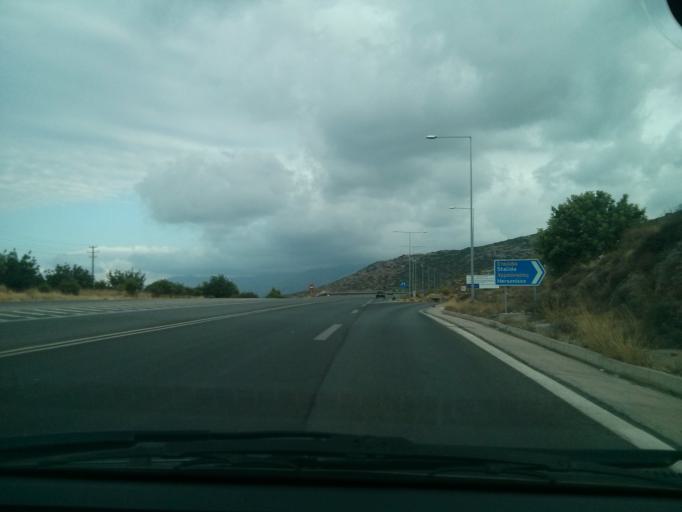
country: GR
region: Crete
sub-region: Nomos Irakleiou
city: Limin Khersonisou
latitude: 35.3011
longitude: 25.3981
